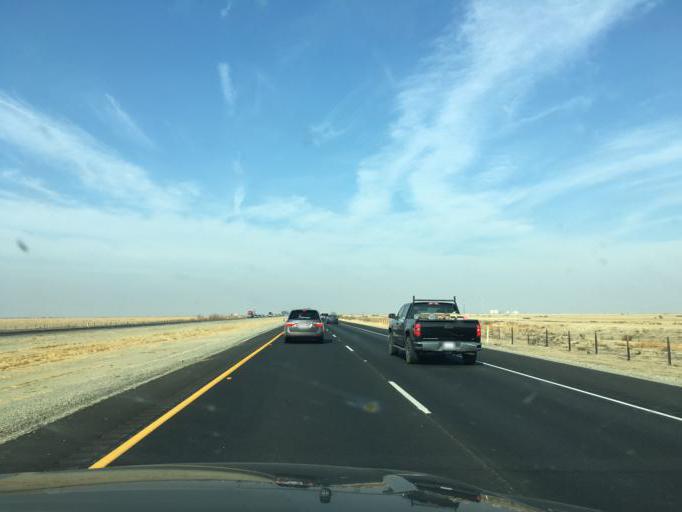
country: US
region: California
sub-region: Kern County
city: Lost Hills
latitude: 35.7185
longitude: -119.7291
